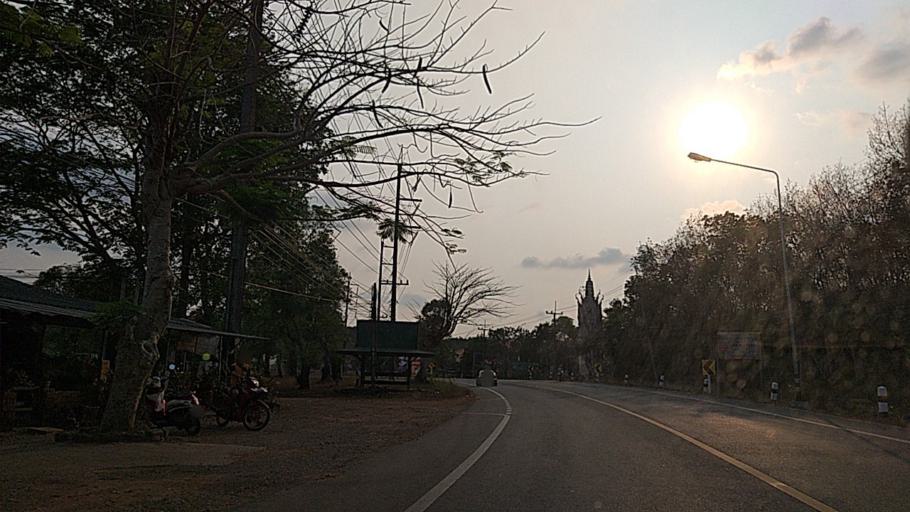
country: TH
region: Trat
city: Khao Saming
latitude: 12.2880
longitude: 102.3140
